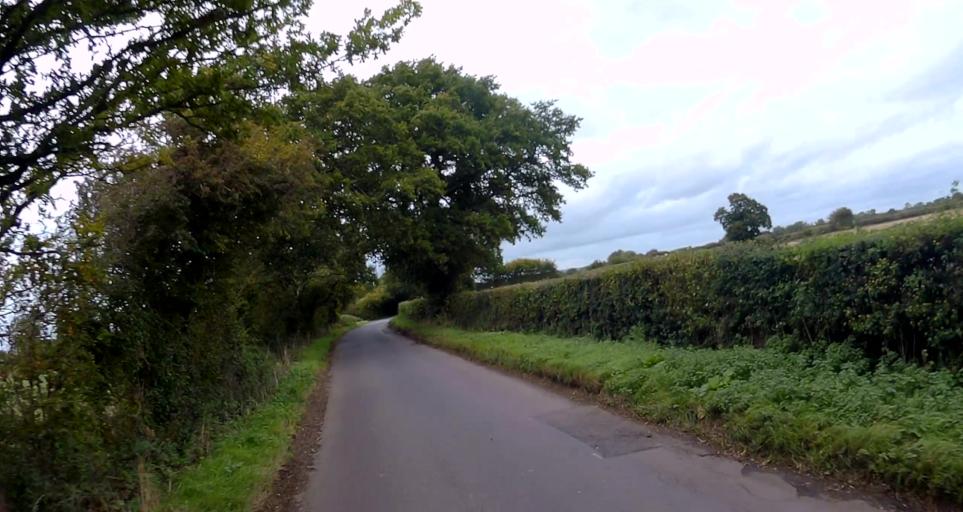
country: GB
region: England
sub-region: Hampshire
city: Four Marks
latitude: 51.1434
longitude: -1.0861
